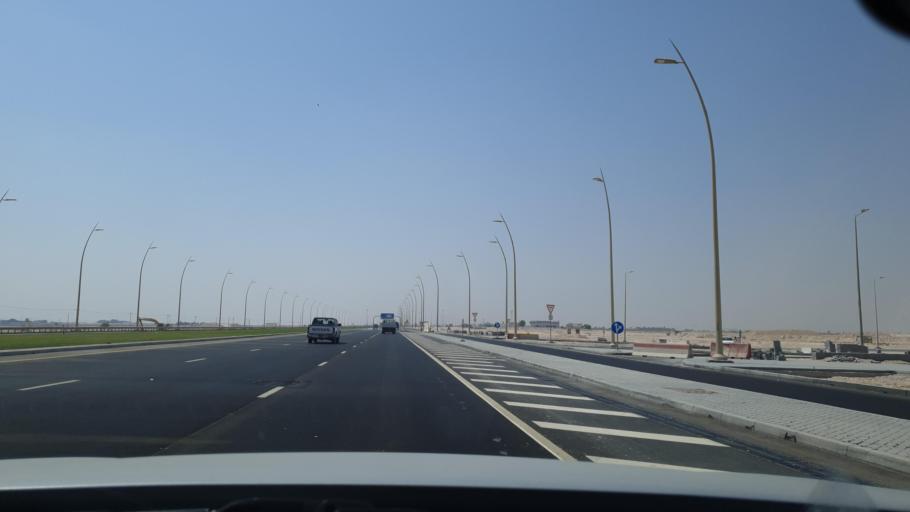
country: QA
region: Al Khawr
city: Al Khawr
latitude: 25.6580
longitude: 51.4641
